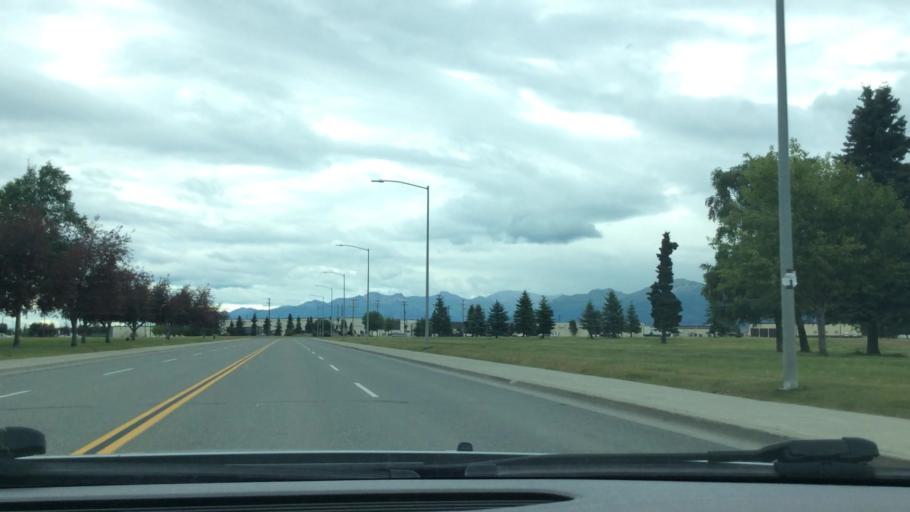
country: US
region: Alaska
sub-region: Anchorage Municipality
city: Anchorage
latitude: 61.2359
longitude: -149.8542
